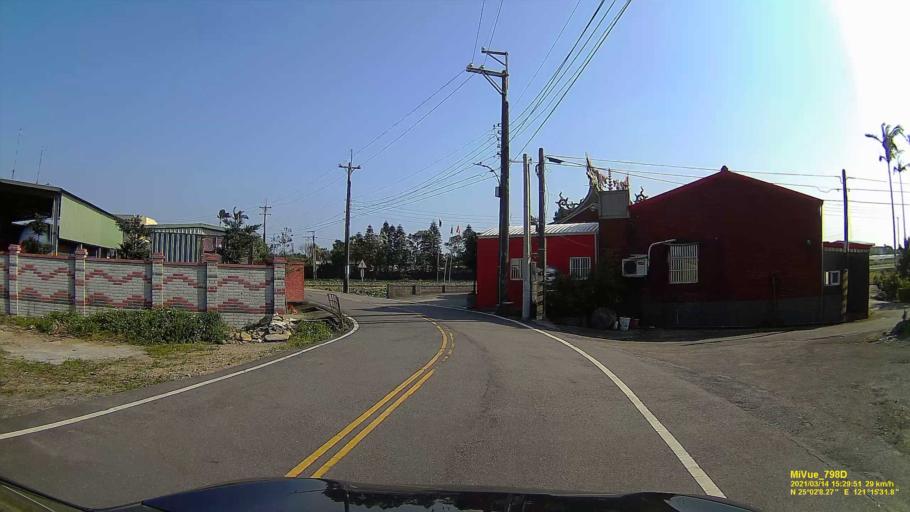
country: TW
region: Taiwan
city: Taoyuan City
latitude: 25.0355
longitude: 121.2589
